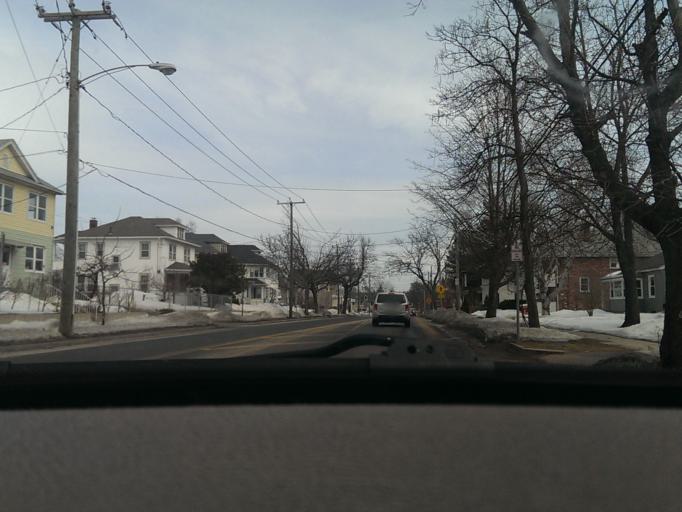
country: US
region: Massachusetts
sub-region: Hampden County
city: Ludlow
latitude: 42.1529
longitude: -72.4916
